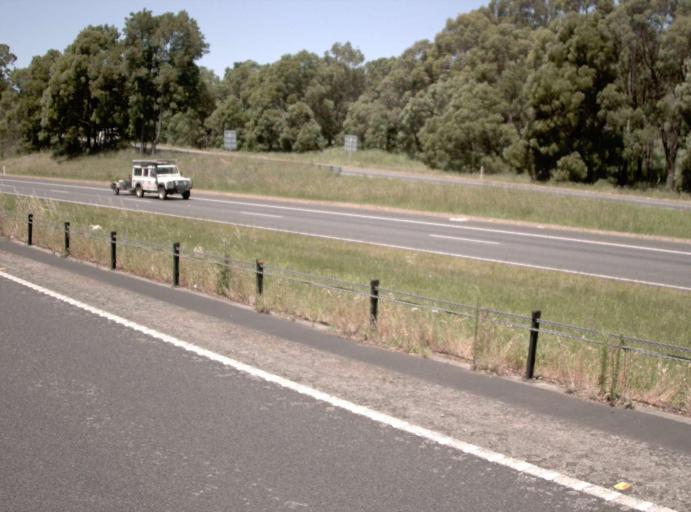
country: AU
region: Victoria
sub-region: Baw Baw
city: Warragul
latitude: -38.1714
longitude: 145.9291
